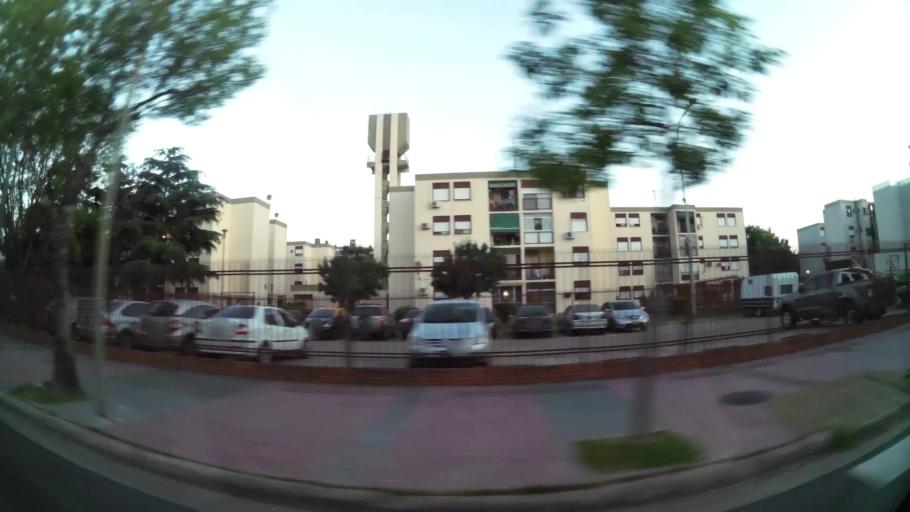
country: AR
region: Buenos Aires F.D.
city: Villa Lugano
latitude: -34.6820
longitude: -58.4708
